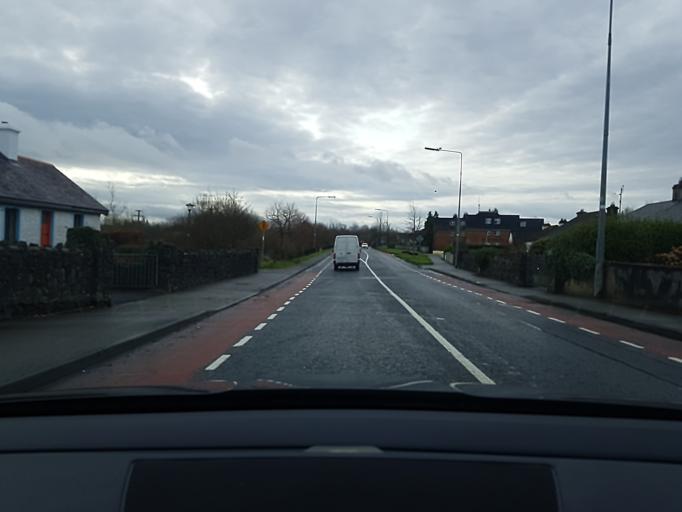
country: IE
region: Connaught
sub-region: Maigh Eo
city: Castlebar
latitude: 53.8465
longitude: -9.2894
